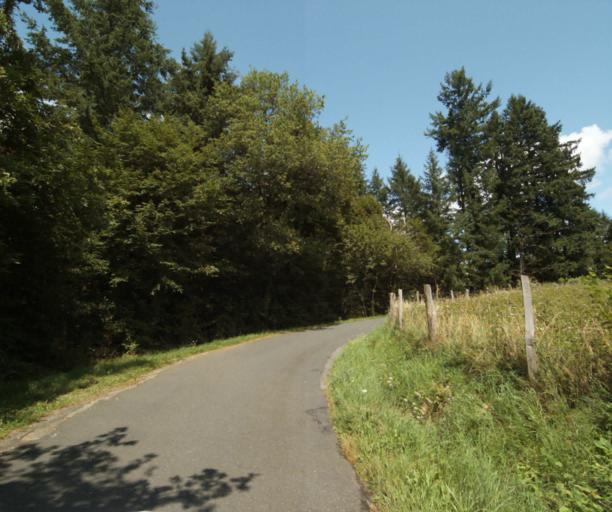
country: FR
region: Limousin
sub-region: Departement de la Correze
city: Sainte-Fortunade
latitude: 45.2042
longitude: 1.8348
